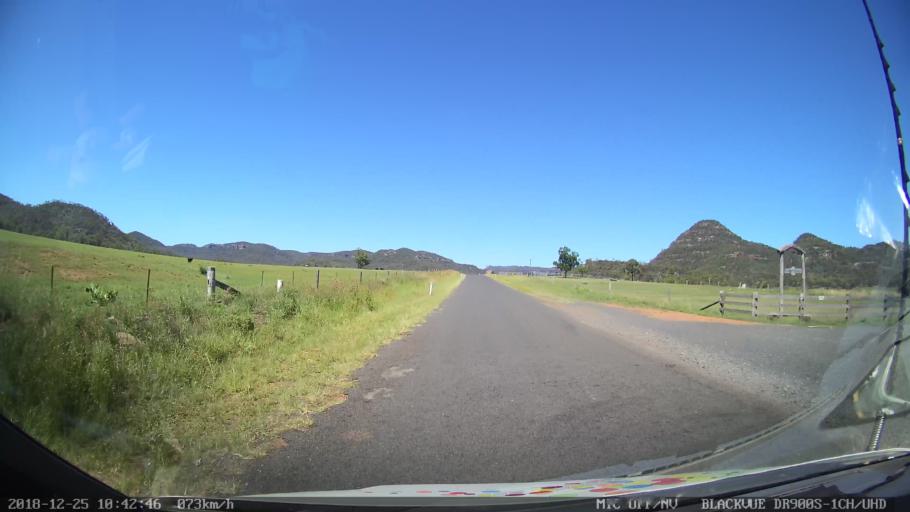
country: AU
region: New South Wales
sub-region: Upper Hunter Shire
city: Merriwa
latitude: -32.4177
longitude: 150.3198
